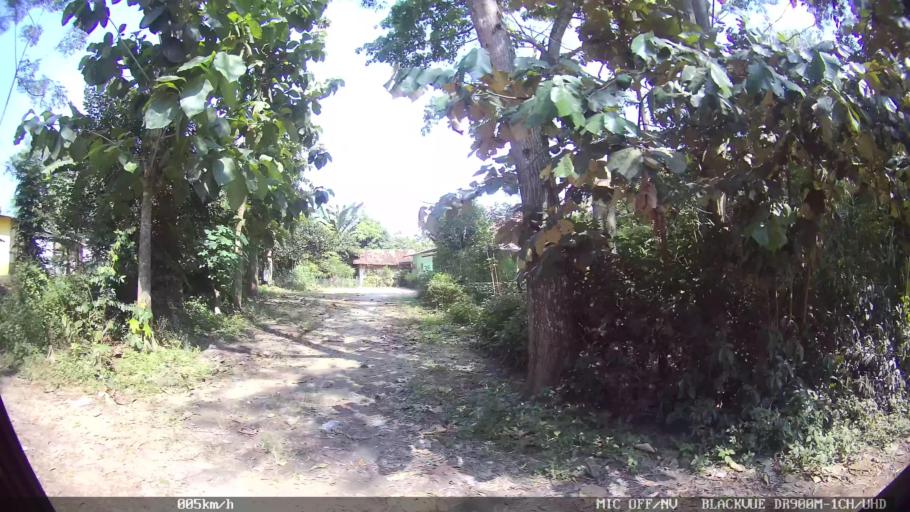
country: ID
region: Lampung
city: Natar
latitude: -5.2535
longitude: 105.1940
